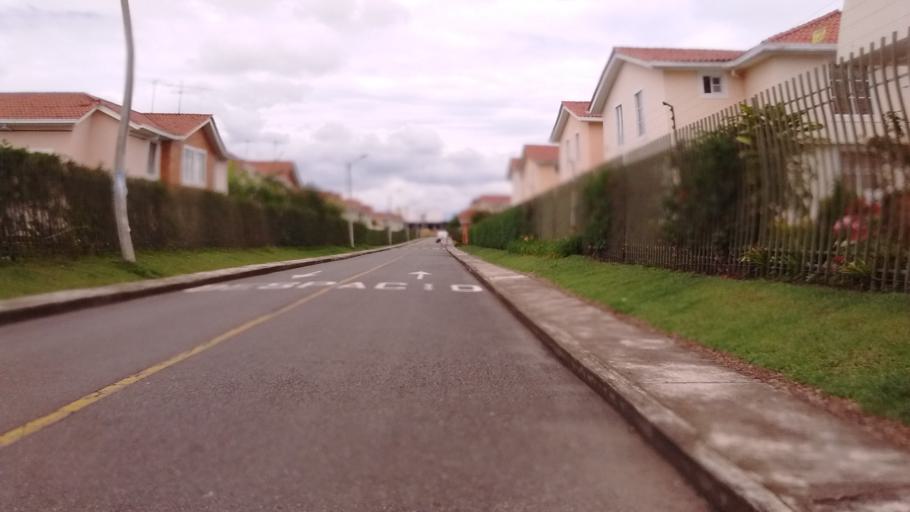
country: CO
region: Cauca
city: Popayan
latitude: 2.4782
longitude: -76.5801
